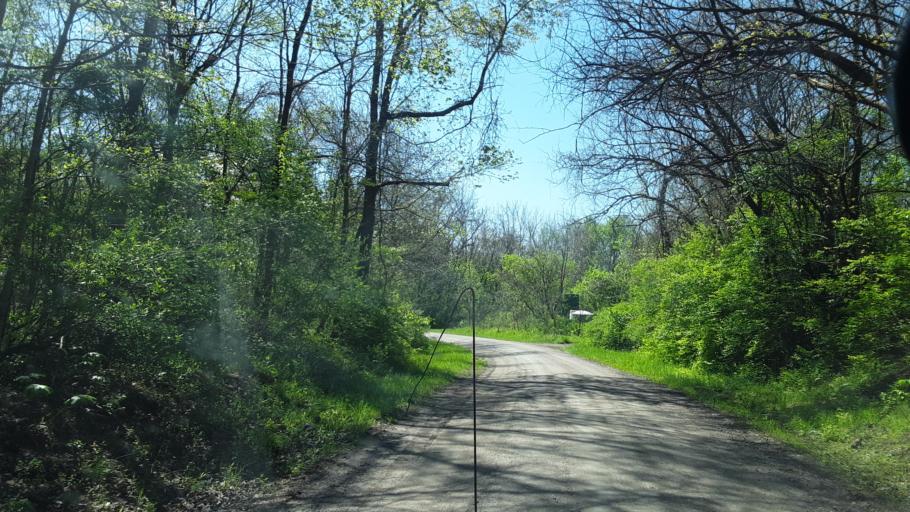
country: US
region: Ohio
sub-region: Noble County
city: Caldwell
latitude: 39.7851
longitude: -81.6258
